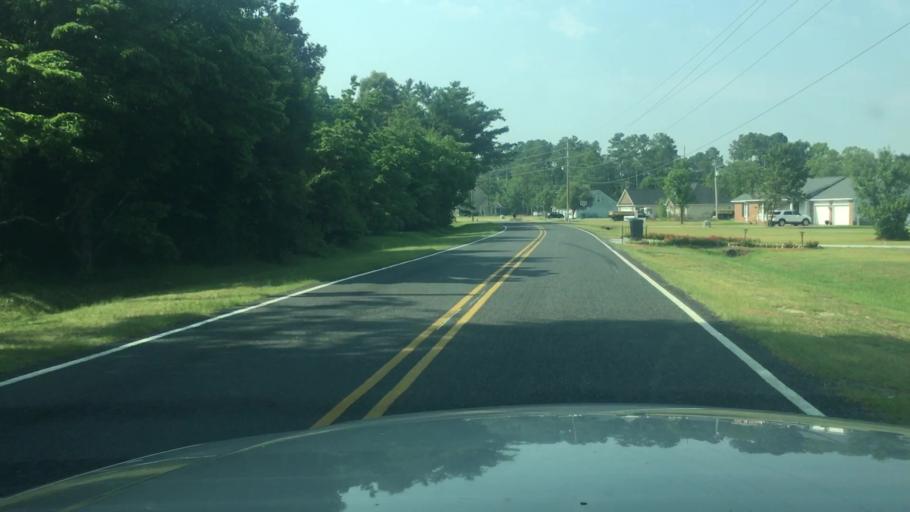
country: US
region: North Carolina
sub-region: Cumberland County
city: Hope Mills
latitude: 34.9054
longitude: -78.8720
